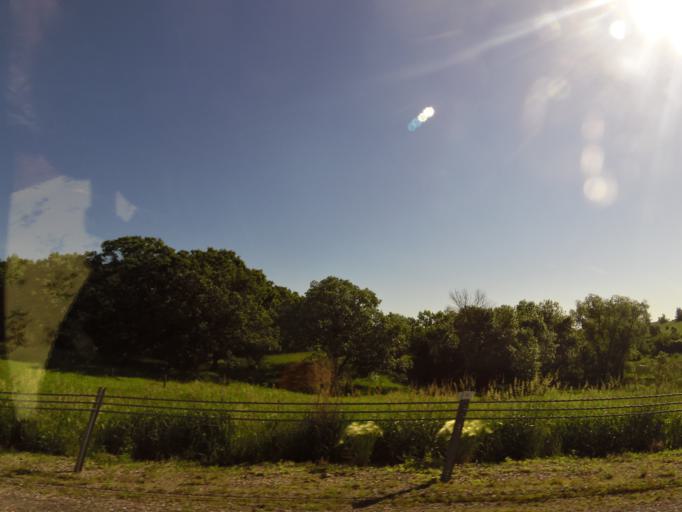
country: US
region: Minnesota
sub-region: Otter Tail County
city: Fergus Falls
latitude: 46.2122
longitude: -96.0244
